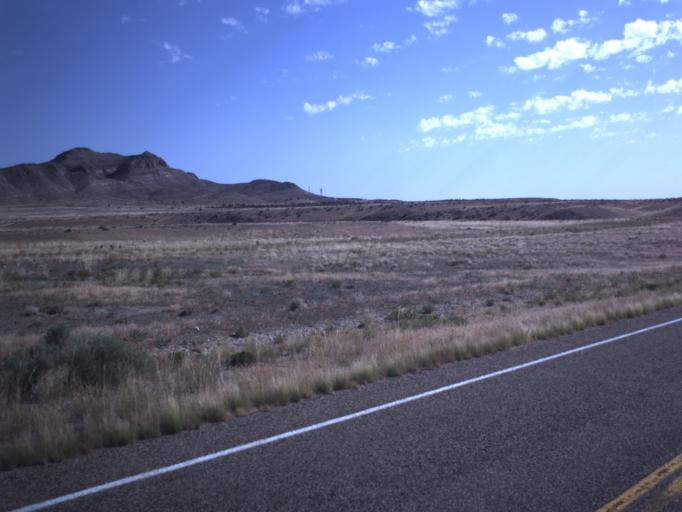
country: US
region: Utah
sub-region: Beaver County
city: Milford
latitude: 38.8051
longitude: -112.8825
